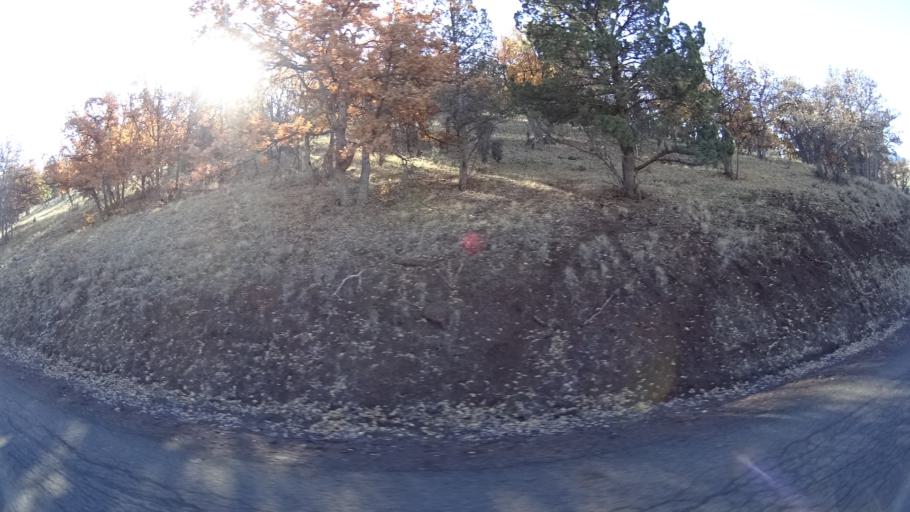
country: US
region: California
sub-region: Siskiyou County
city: Montague
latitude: 41.9152
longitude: -122.4394
